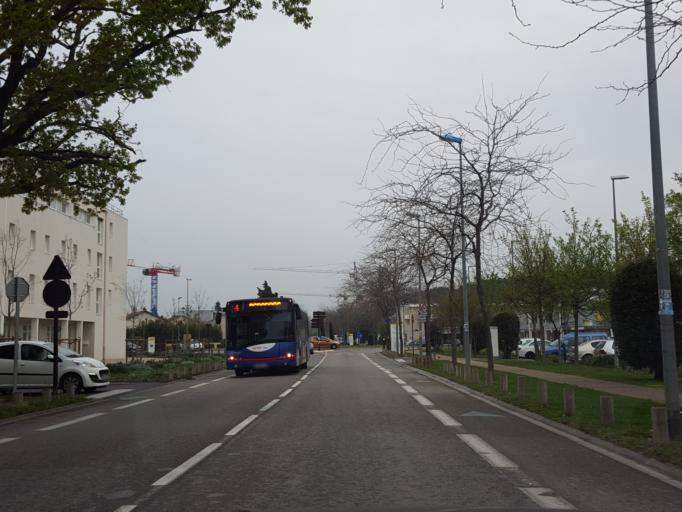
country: FR
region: Provence-Alpes-Cote d'Azur
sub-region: Departement du Vaucluse
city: Montfavet
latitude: 43.9157
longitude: 4.8903
